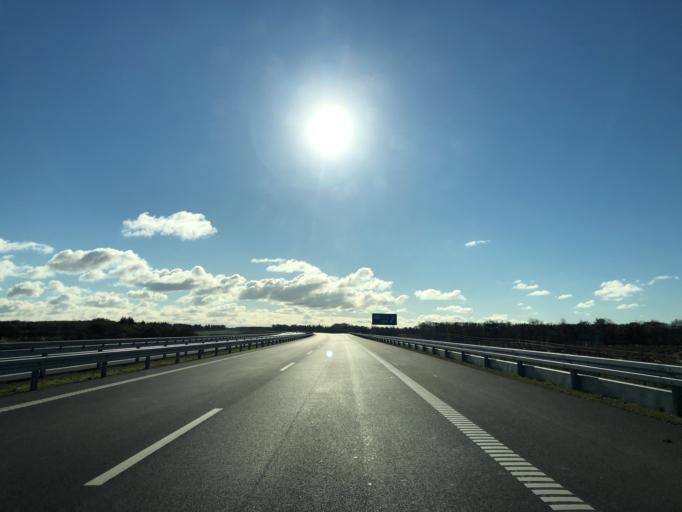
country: DK
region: Central Jutland
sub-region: Herning Kommune
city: Avlum
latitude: 56.3006
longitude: 8.7264
